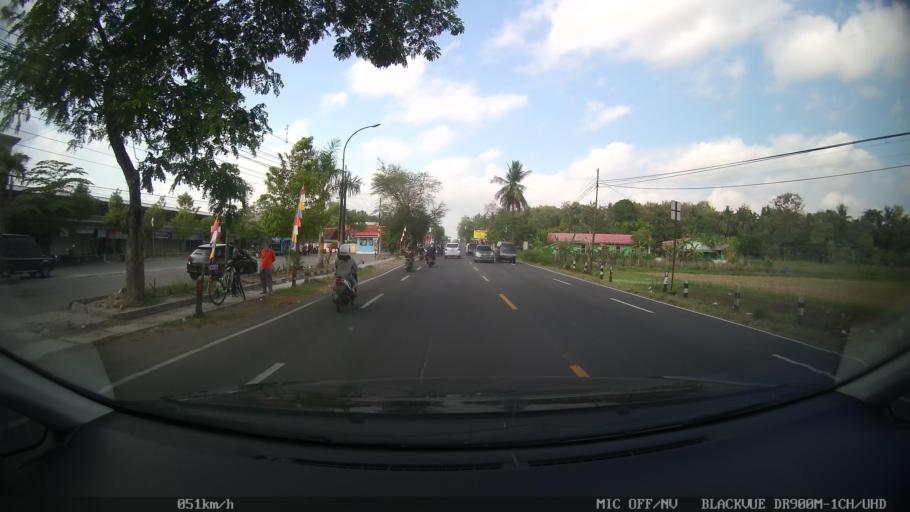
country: ID
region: Daerah Istimewa Yogyakarta
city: Srandakan
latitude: -7.8469
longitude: 110.2179
